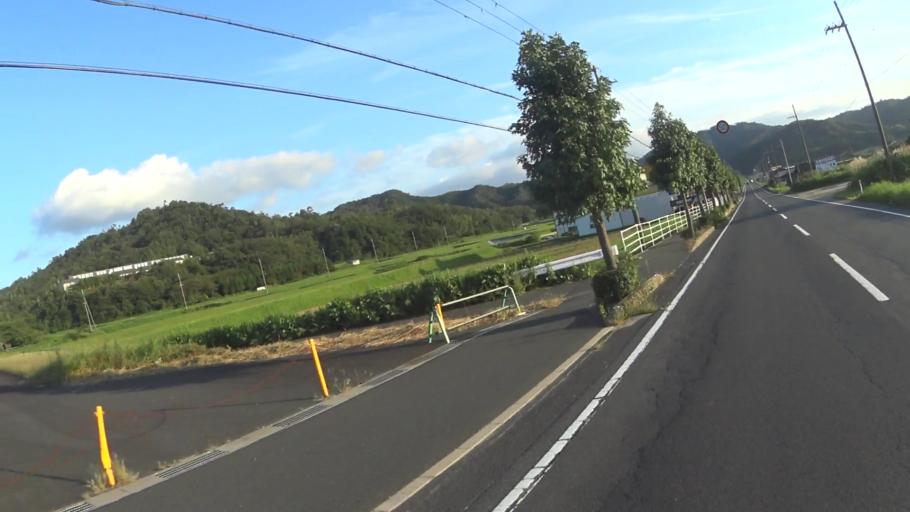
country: JP
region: Kyoto
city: Miyazu
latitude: 35.5758
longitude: 135.0987
